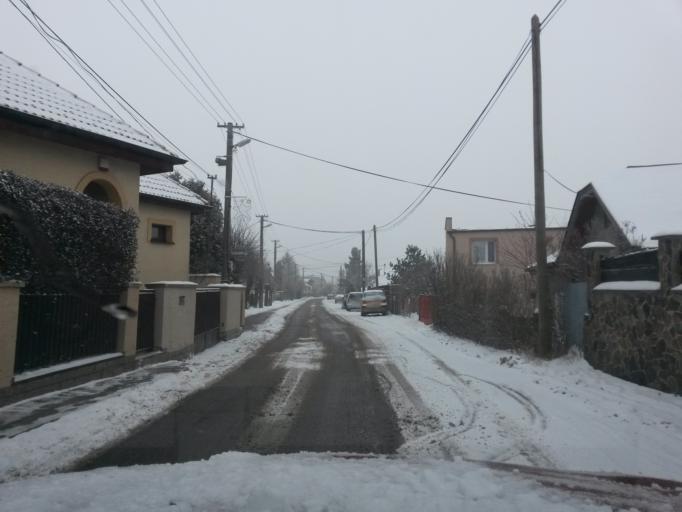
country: SK
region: Kosicky
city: Kosice
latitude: 48.7332
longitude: 21.2982
